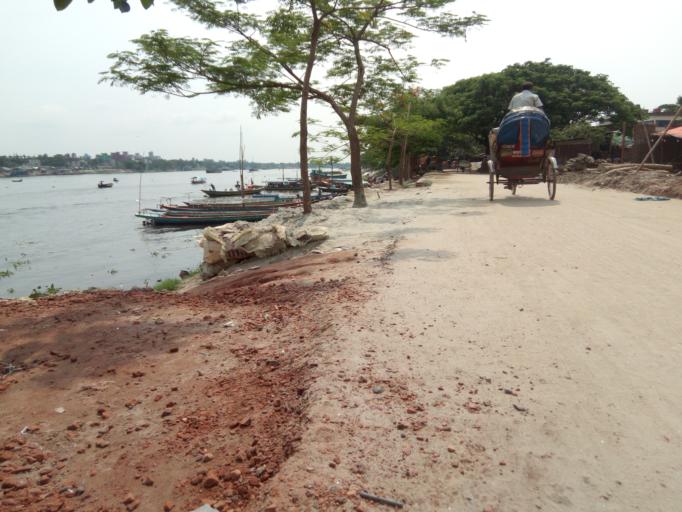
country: BD
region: Dhaka
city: Azimpur
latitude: 23.7085
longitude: 90.3795
